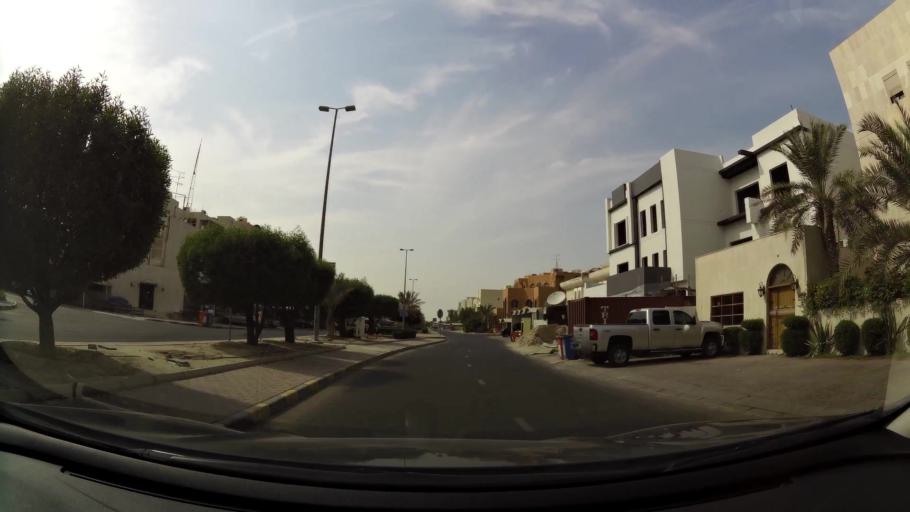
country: KW
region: Al Asimah
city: Ash Shamiyah
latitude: 29.3365
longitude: 47.9671
